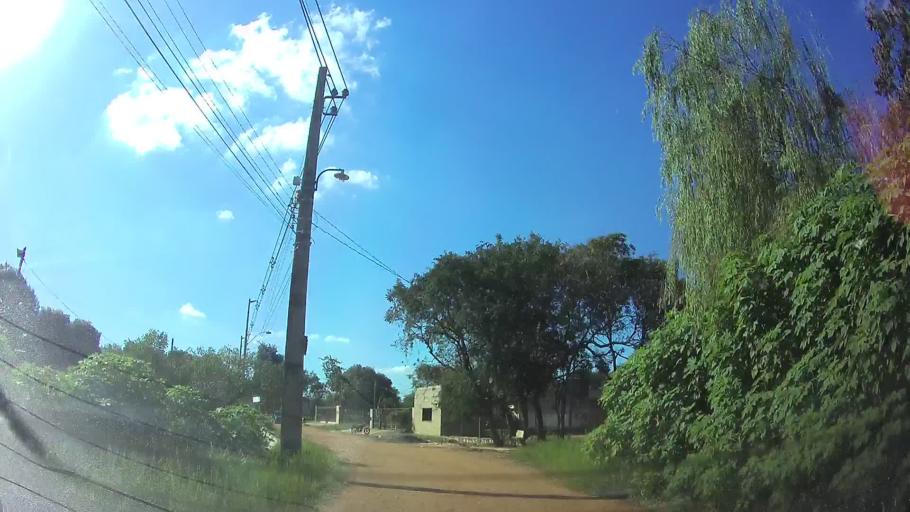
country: PY
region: Central
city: Limpio
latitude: -25.2460
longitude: -57.4744
